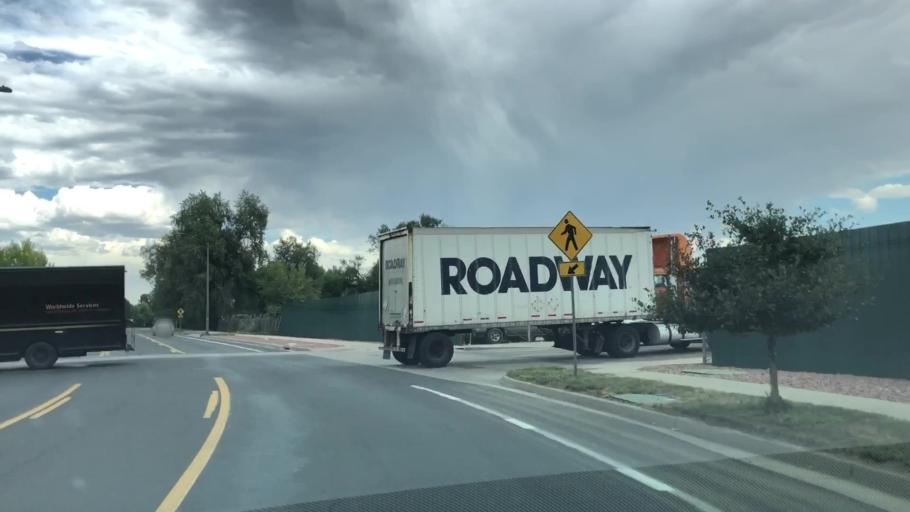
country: US
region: Colorado
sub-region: Larimer County
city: Fort Collins
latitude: 40.5831
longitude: -105.0536
